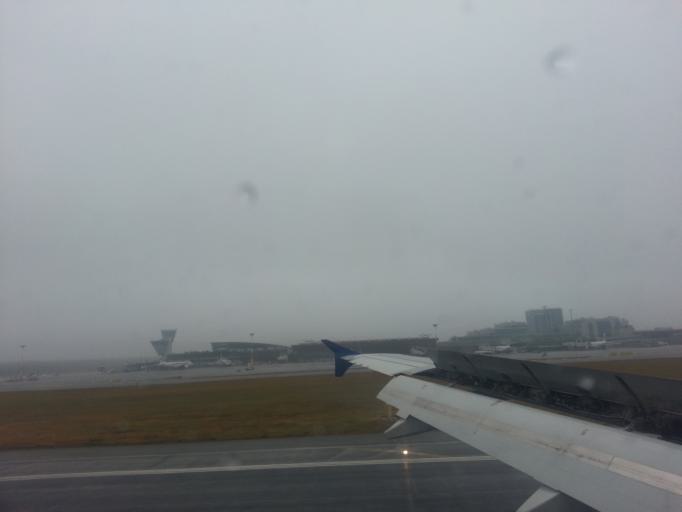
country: FI
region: Uusimaa
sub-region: Helsinki
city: Vantaa
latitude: 60.3226
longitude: 24.9614
